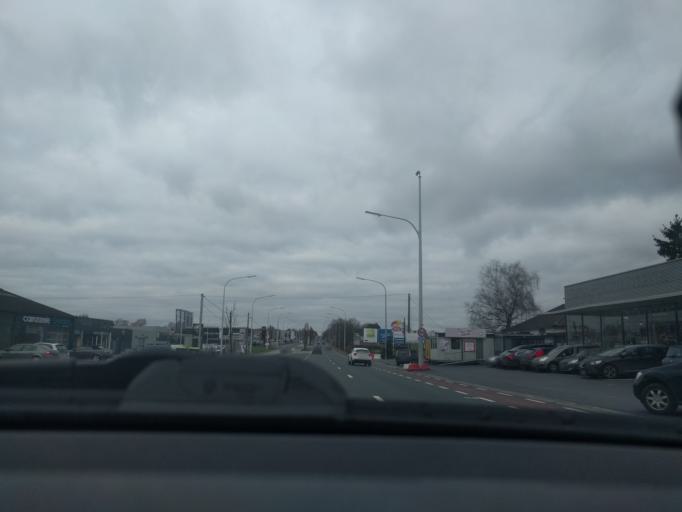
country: BE
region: Wallonia
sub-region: Province de Namur
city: Namur
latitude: 50.4243
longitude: 4.9323
